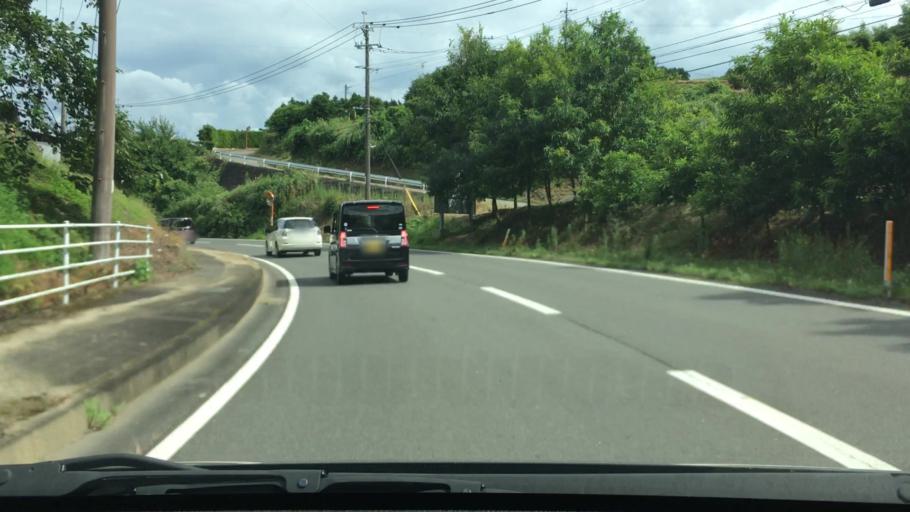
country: JP
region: Nagasaki
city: Togitsu
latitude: 32.9176
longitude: 129.7849
